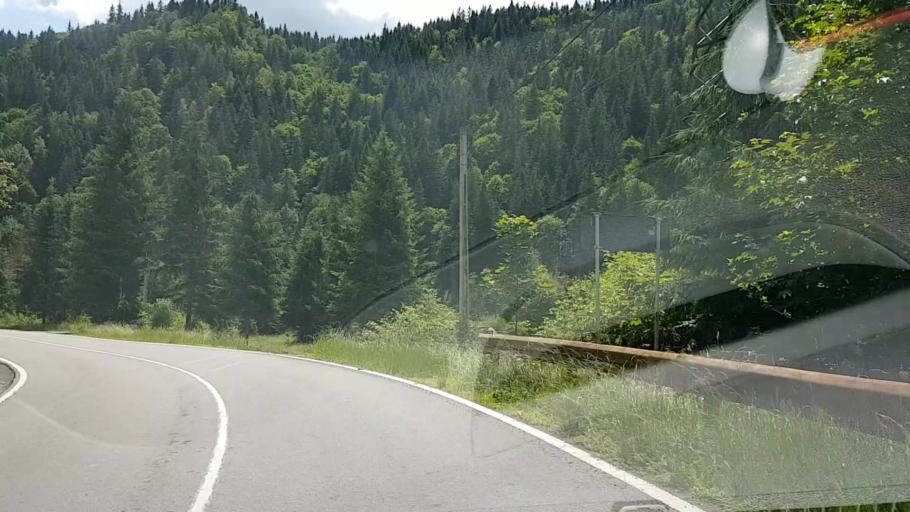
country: RO
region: Suceava
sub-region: Comuna Crucea
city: Crucea
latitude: 47.3816
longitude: 25.5750
